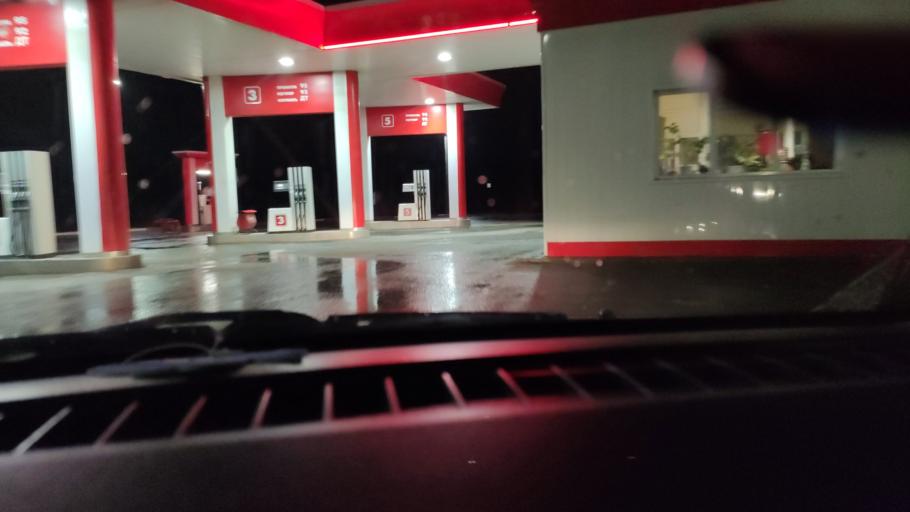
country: RU
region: Perm
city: Krasnokamsk
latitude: 58.1022
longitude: 55.7512
